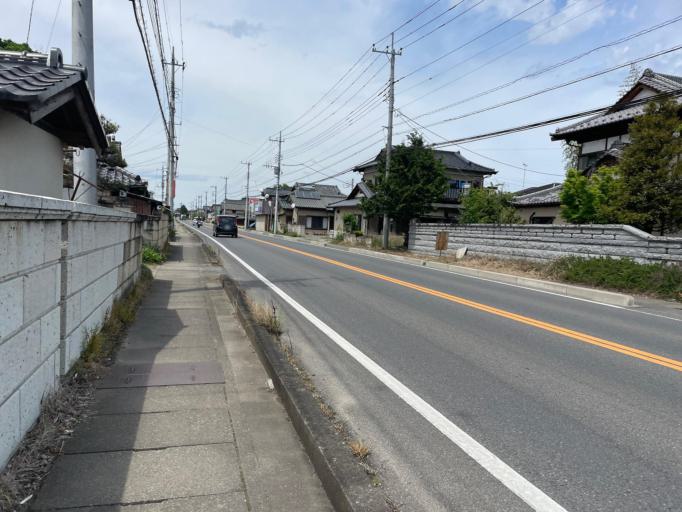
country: JP
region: Tochigi
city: Mibu
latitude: 36.4526
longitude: 139.7754
